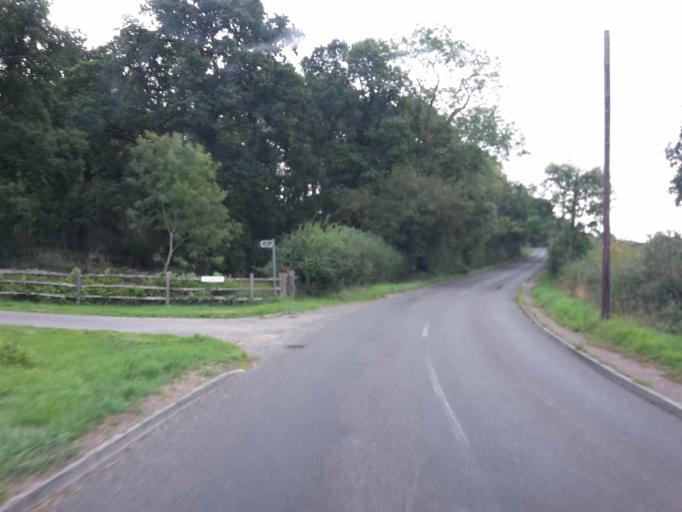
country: GB
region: England
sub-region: West Sussex
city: Rudgwick
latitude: 51.0571
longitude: -0.4366
